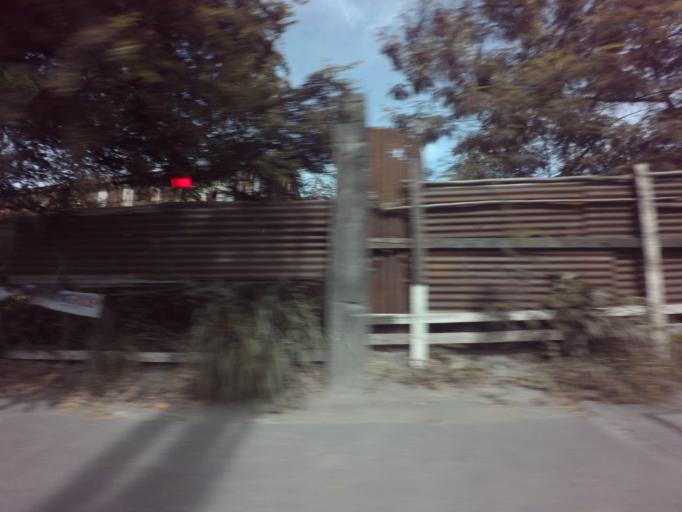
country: PH
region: Calabarzon
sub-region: Province of Rizal
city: Pateros
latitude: 14.5451
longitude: 121.0887
